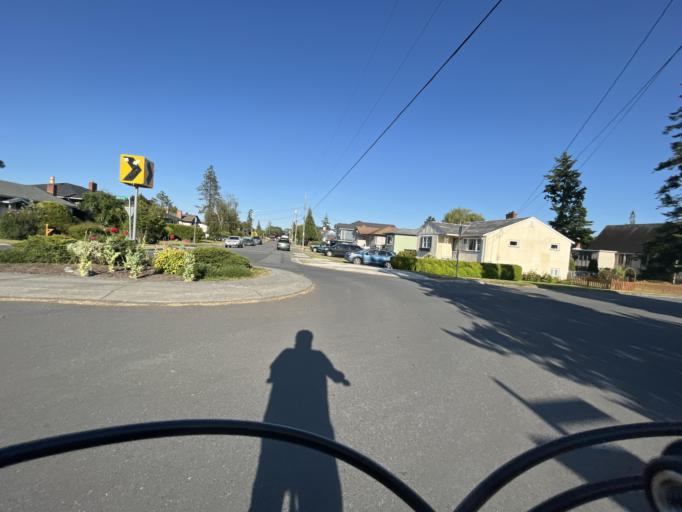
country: CA
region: British Columbia
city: Oak Bay
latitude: 48.4377
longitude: -123.3250
